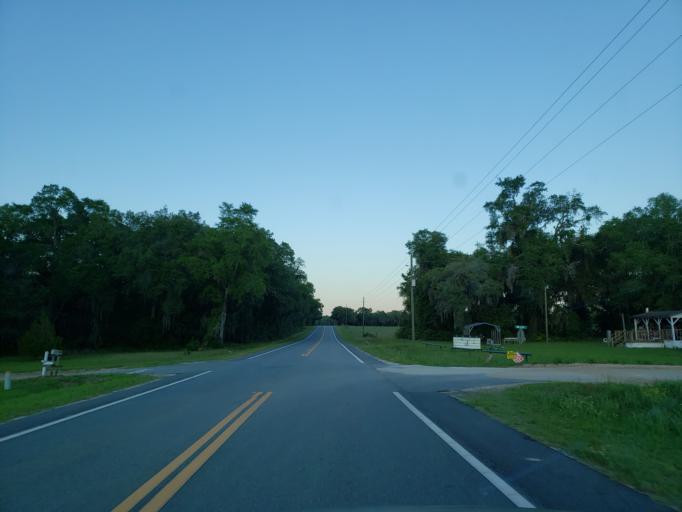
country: US
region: Georgia
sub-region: Echols County
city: Statenville
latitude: 30.5807
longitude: -83.1915
